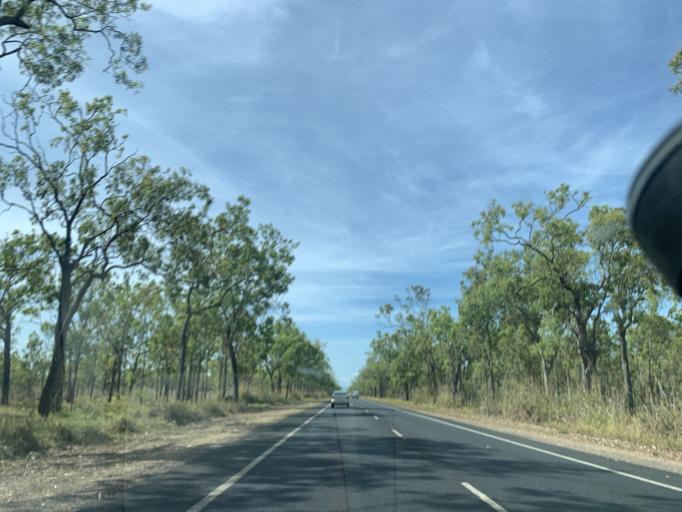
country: AU
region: Queensland
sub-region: Tablelands
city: Mareeba
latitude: -17.0415
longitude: 145.4297
